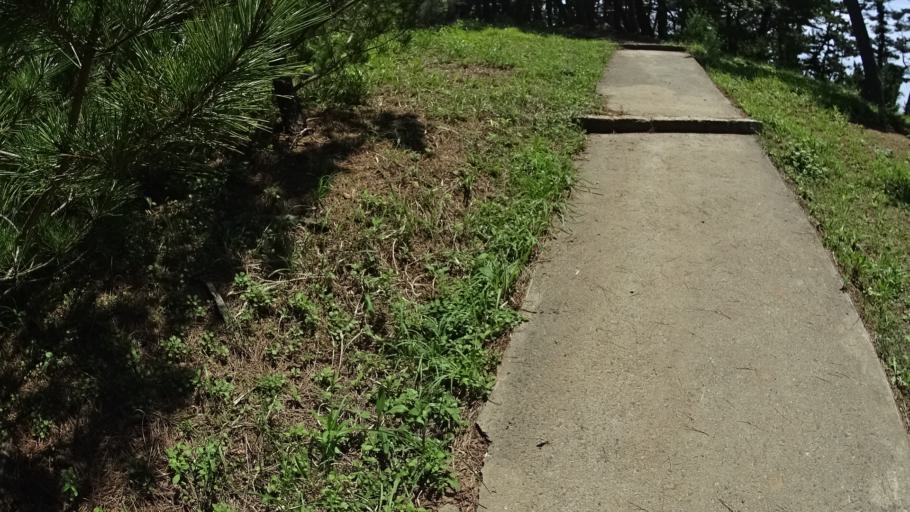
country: JP
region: Iwate
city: Ofunato
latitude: 38.8319
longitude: 141.6241
